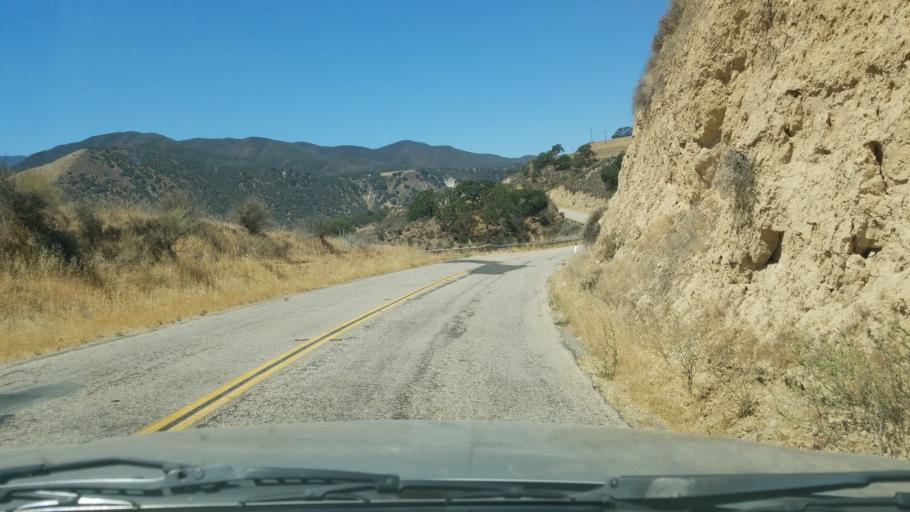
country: US
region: California
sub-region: Monterey County
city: Greenfield
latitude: 36.2701
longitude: -121.3520
